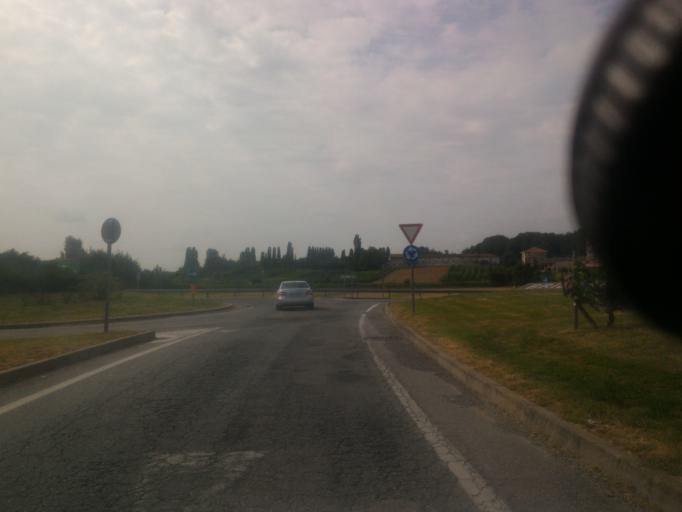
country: IT
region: Piedmont
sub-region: Provincia di Torino
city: Bricherasio
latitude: 44.8328
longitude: 7.3060
